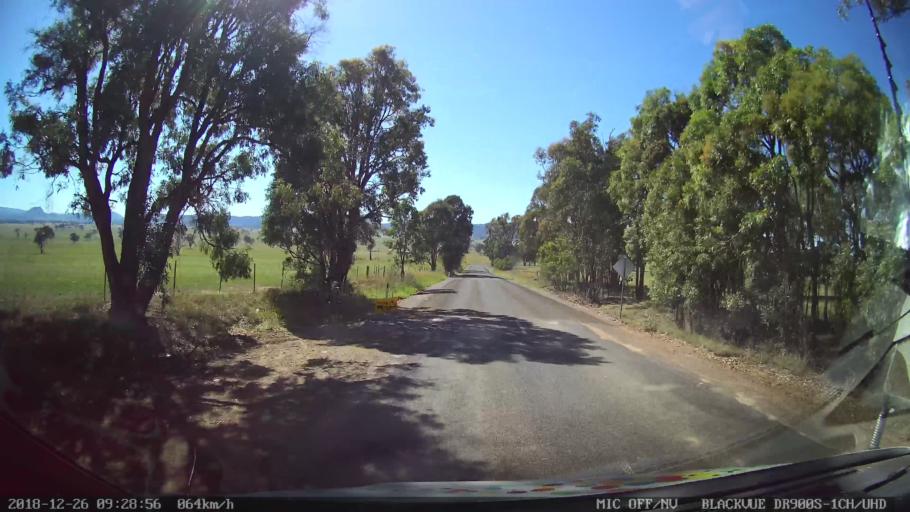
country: AU
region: New South Wales
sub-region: Mid-Western Regional
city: Kandos
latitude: -32.8492
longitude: 150.0241
